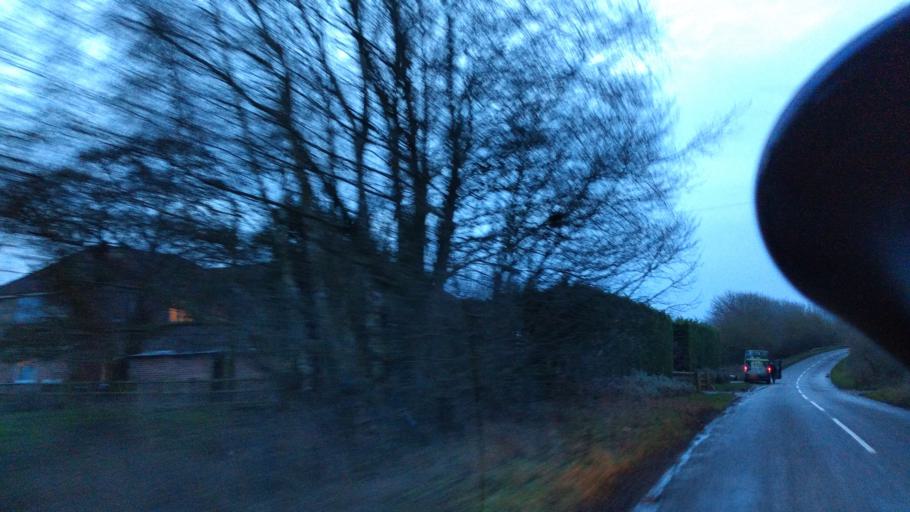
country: GB
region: England
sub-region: Oxfordshire
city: Shrivenham
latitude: 51.6044
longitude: -1.6663
